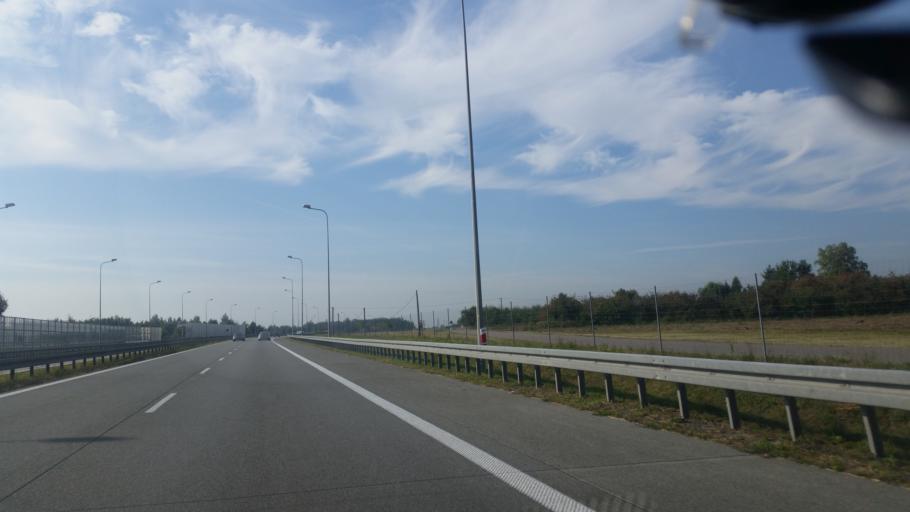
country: PL
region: Lodz Voivodeship
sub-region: Powiat skierniewicki
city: Kowiesy
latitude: 51.8661
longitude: 20.3839
